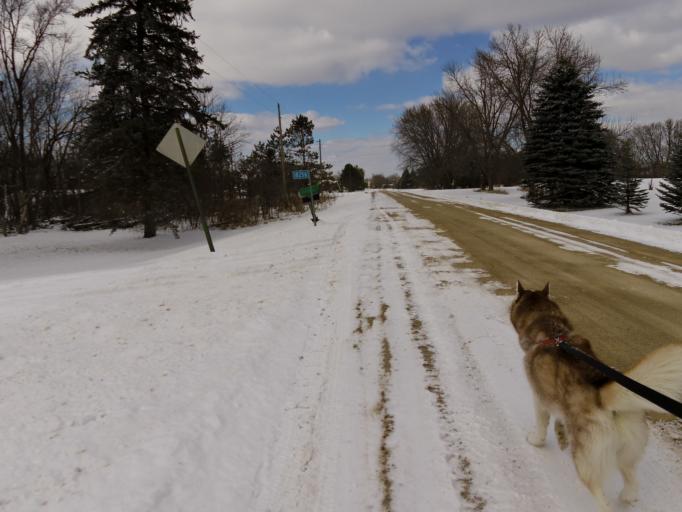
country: US
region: Minnesota
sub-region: Scott County
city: Prior Lake
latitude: 44.6847
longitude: -93.4527
